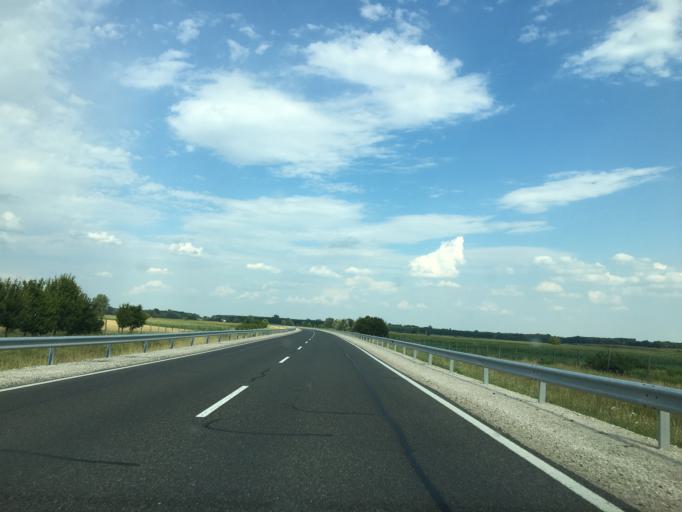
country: HU
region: Tolna
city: Bogyiszlo
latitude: 46.3519
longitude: 18.8628
